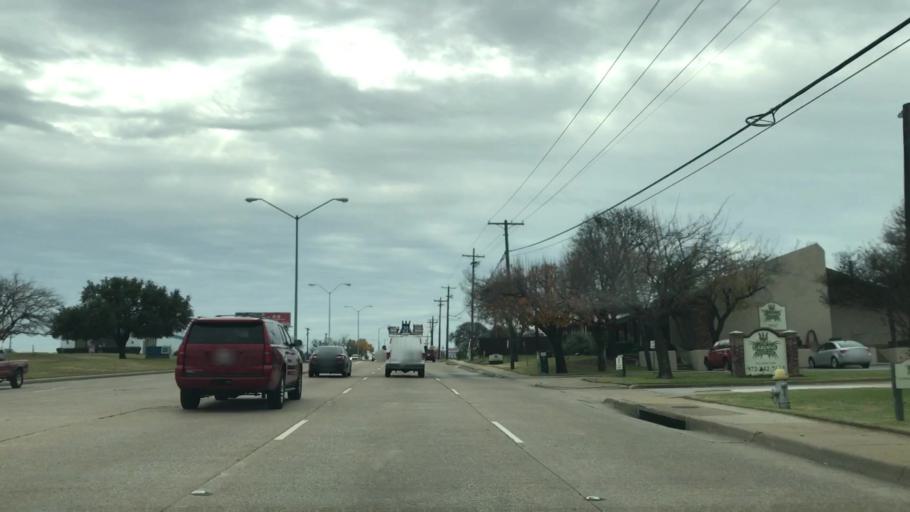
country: US
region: Texas
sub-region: Dallas County
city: Carrollton
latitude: 32.9662
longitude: -96.8901
